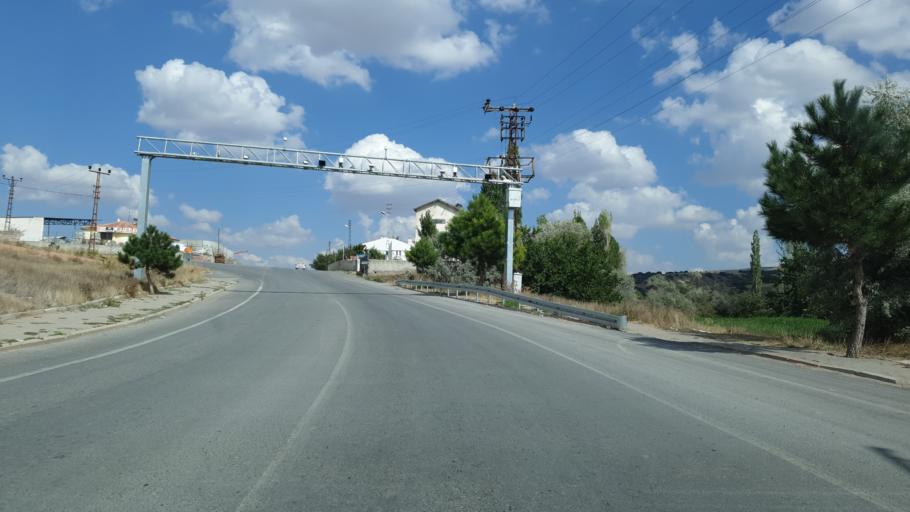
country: TR
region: Kayseri
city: Felahiye
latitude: 39.0939
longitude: 35.5724
